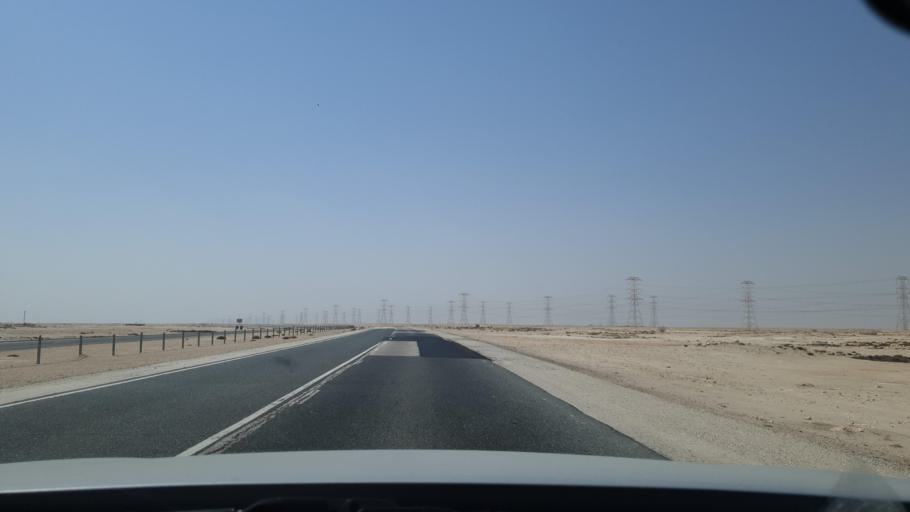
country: QA
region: Al Khawr
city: Al Khawr
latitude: 25.7480
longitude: 51.4664
